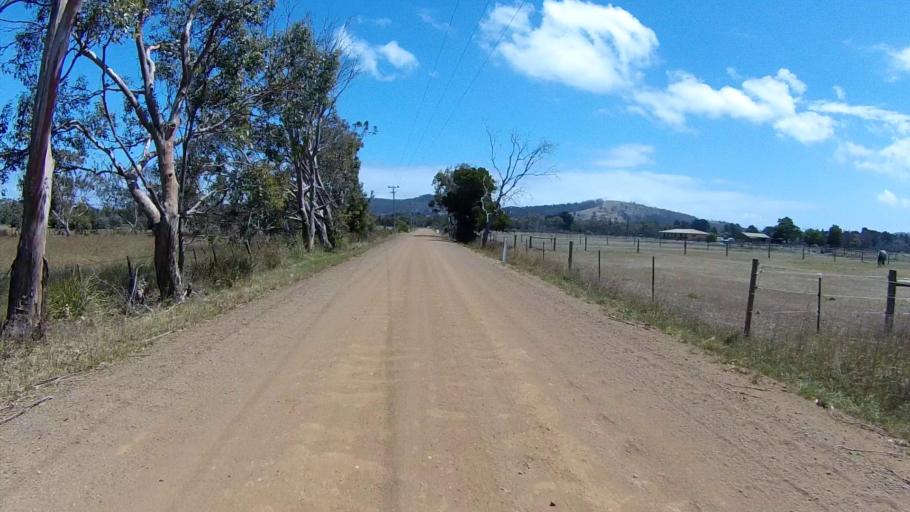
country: AU
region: Tasmania
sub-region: Clarence
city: Sandford
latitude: -42.9343
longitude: 147.5091
